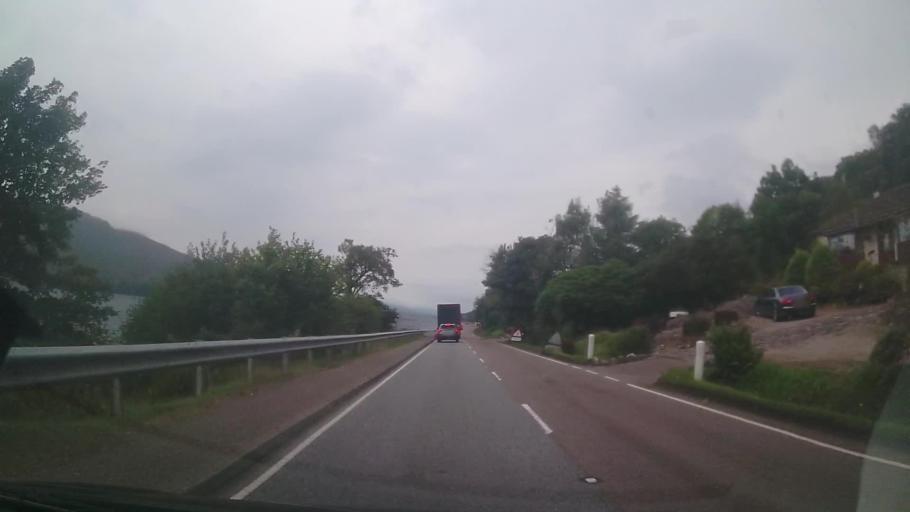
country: GB
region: Scotland
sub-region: Highland
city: Fort William
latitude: 56.7882
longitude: -5.1503
